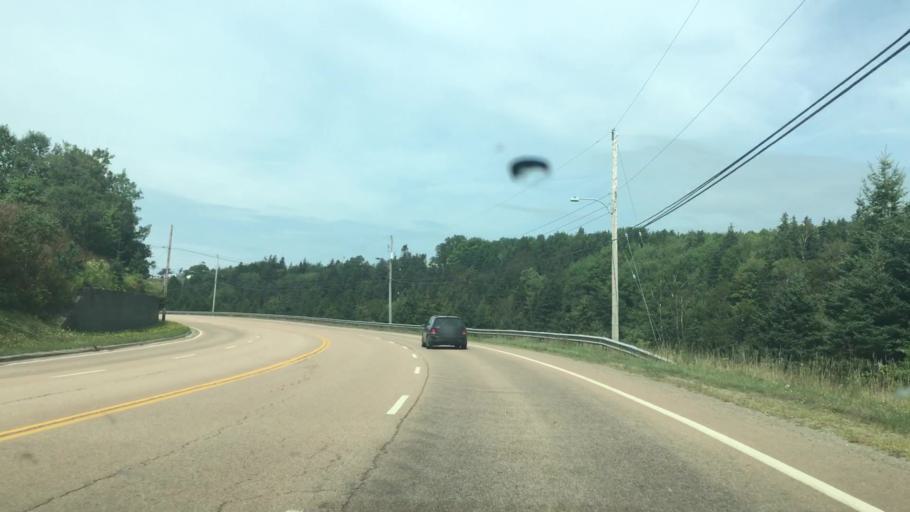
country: CA
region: Nova Scotia
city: Port Hawkesbury
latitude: 45.6245
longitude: -61.3658
